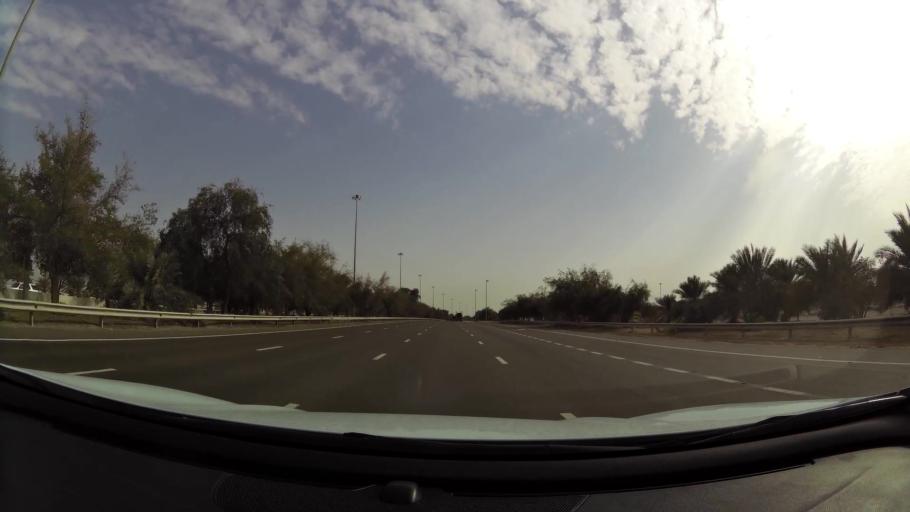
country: AE
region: Abu Dhabi
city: Abu Dhabi
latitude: 24.4551
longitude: 54.6782
